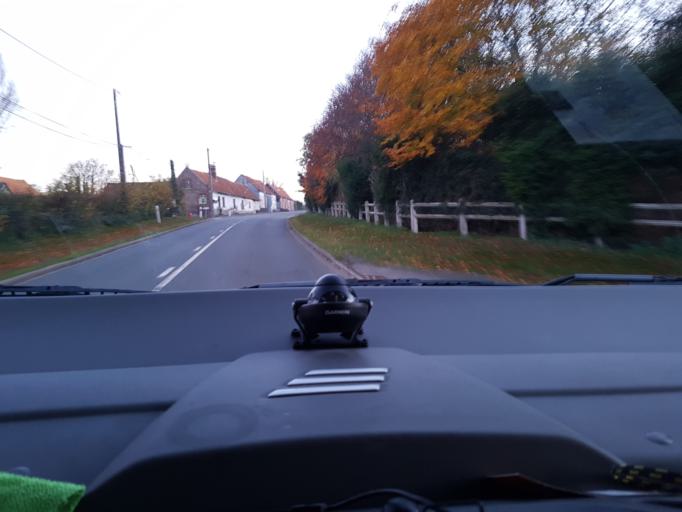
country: FR
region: Picardie
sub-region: Departement de la Somme
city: Rue
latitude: 50.2696
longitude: 1.7439
